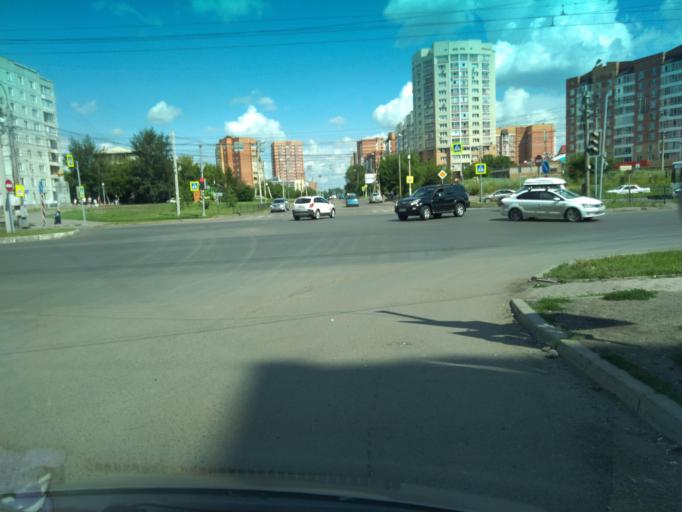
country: RU
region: Krasnoyarskiy
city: Solnechnyy
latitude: 56.0614
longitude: 92.9340
